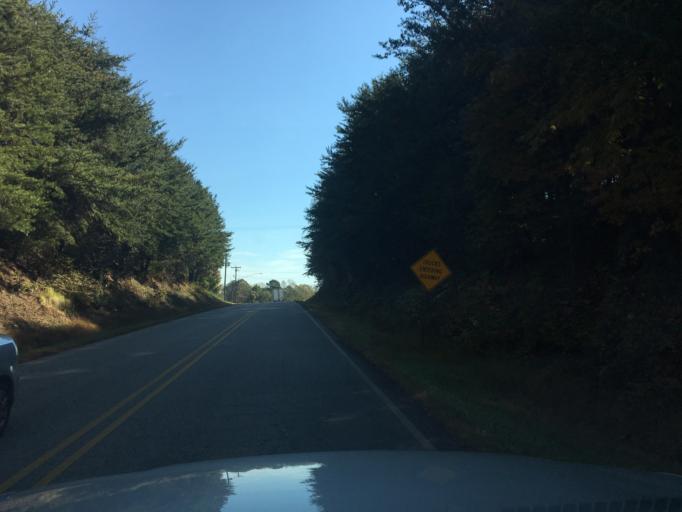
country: US
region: North Carolina
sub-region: Catawba County
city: Conover
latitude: 35.7148
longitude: -81.2575
